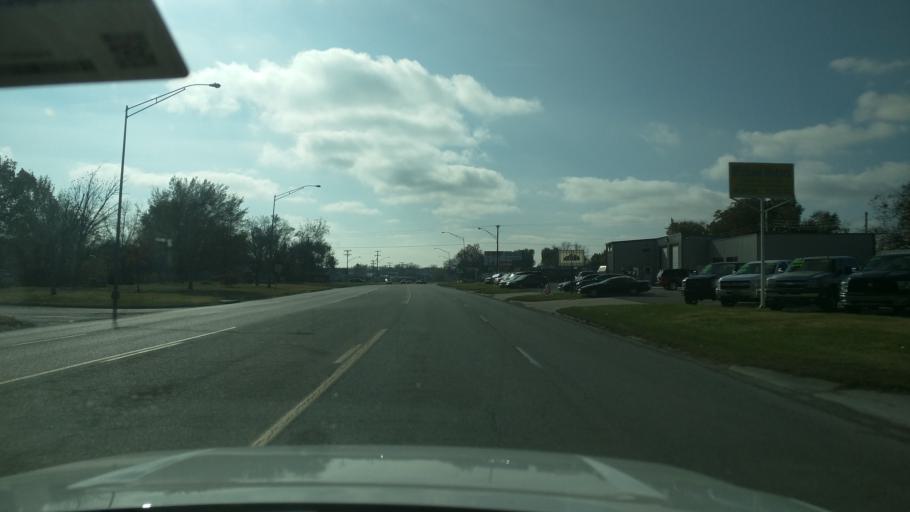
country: US
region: Oklahoma
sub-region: Washington County
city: Dewey
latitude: 36.7927
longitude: -95.9356
